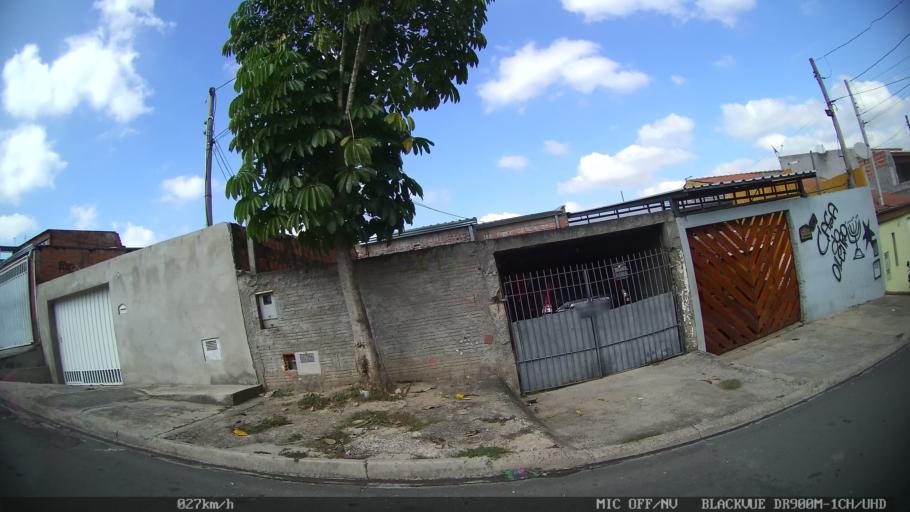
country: BR
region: Sao Paulo
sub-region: Indaiatuba
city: Indaiatuba
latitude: -22.9737
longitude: -47.1800
